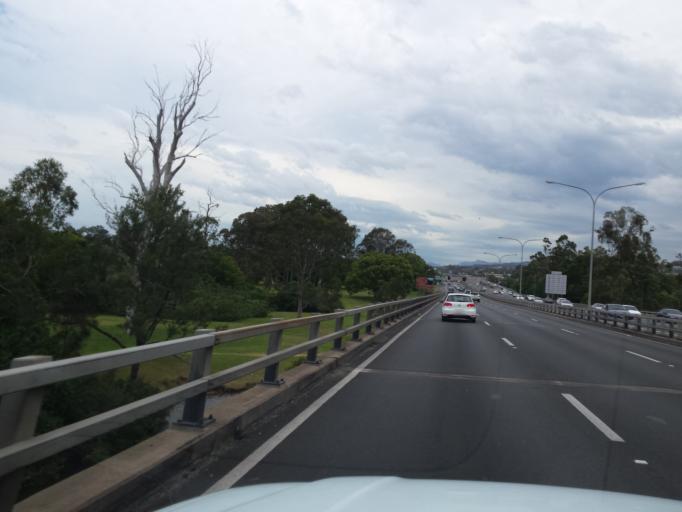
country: AU
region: Queensland
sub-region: Gold Coast
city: Nerang
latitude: -27.9870
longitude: 153.3412
